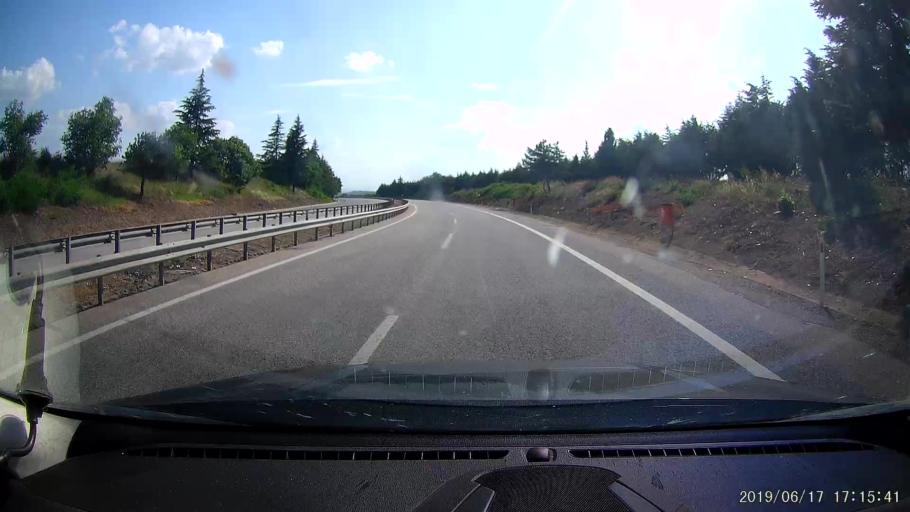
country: GR
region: East Macedonia and Thrace
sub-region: Nomos Evrou
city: Kastanies
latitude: 41.7019
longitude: 26.4908
